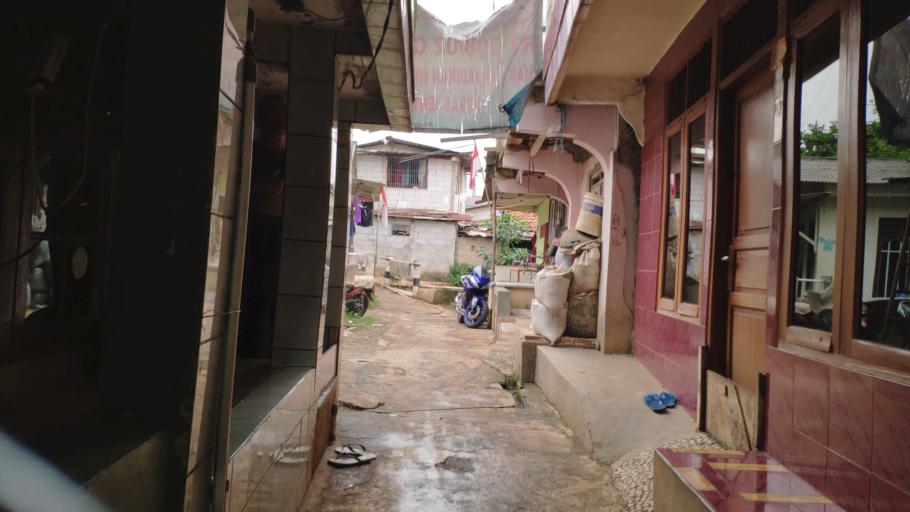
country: ID
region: West Java
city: Pamulang
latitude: -6.2987
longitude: 106.8053
